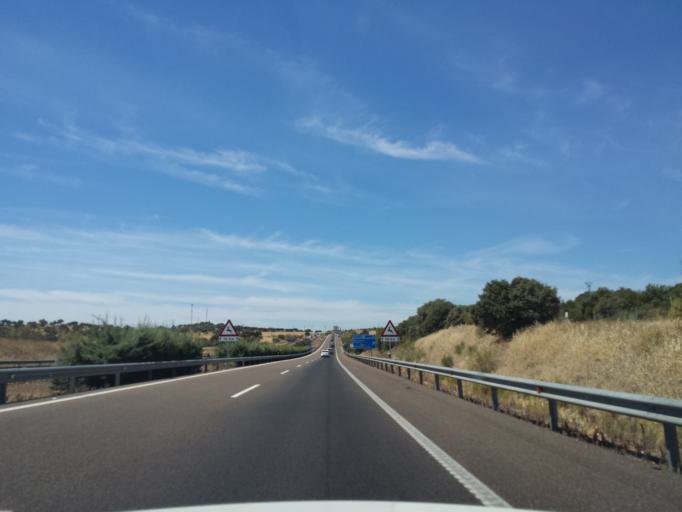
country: ES
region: Extremadura
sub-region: Provincia de Badajoz
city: San Pedro de Merida
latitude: 38.9507
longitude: -6.1683
